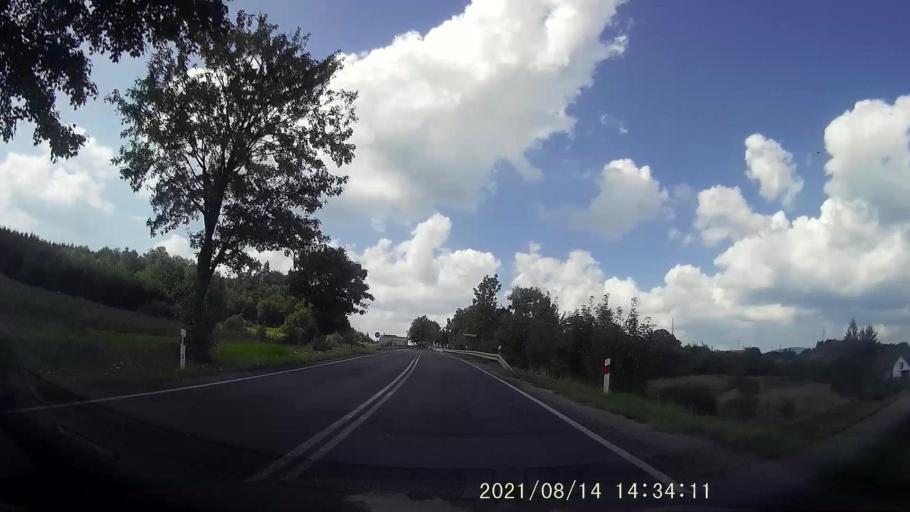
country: PL
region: Lower Silesian Voivodeship
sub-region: Powiat klodzki
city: Nowa Ruda
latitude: 50.5639
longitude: 16.5360
